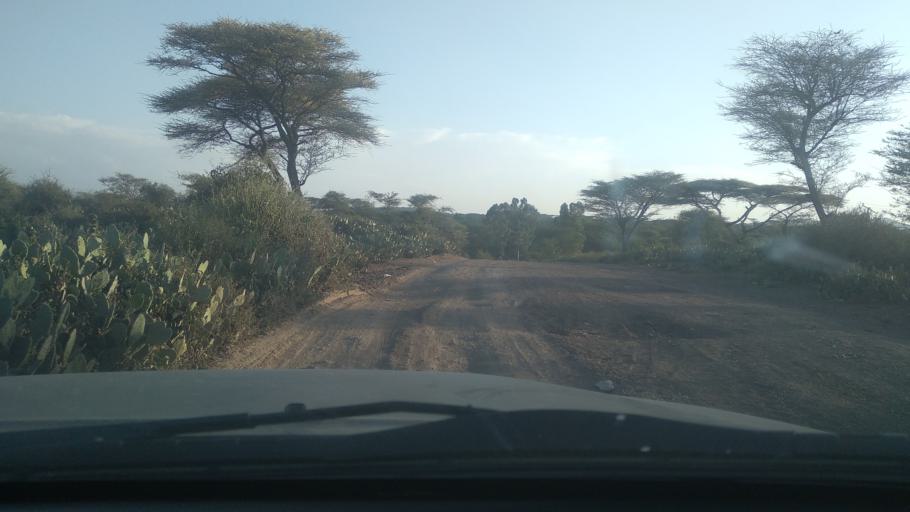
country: ET
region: Oromiya
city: Asbe Teferi
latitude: 9.2863
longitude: 40.8265
